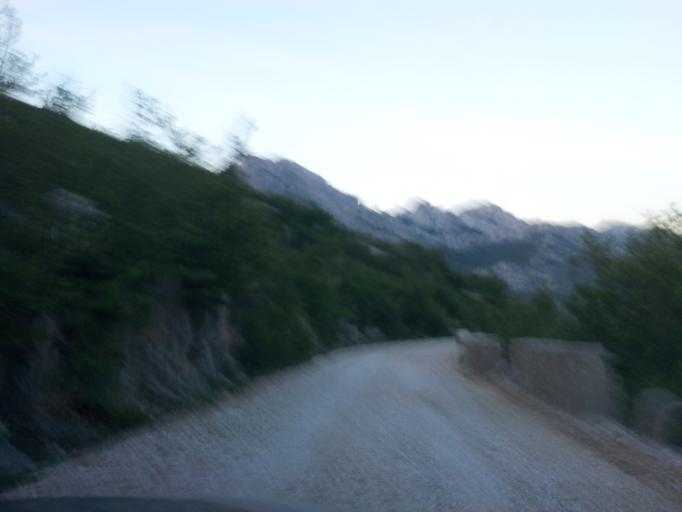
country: HR
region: Zadarska
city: Krusevo
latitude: 44.2521
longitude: 15.6337
